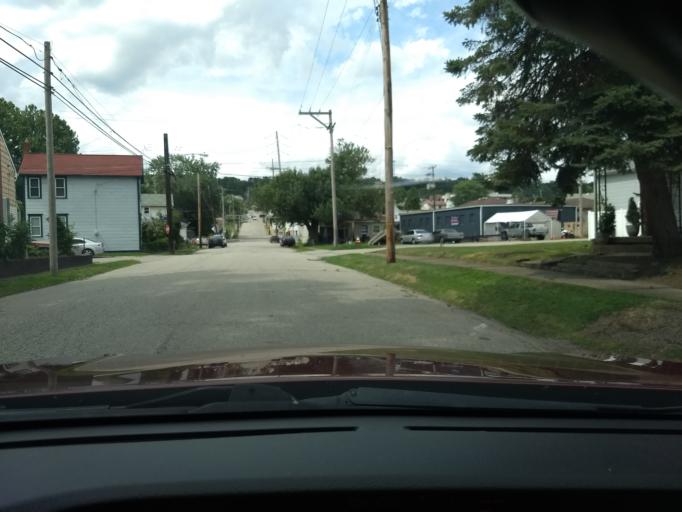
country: US
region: Pennsylvania
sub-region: Allegheny County
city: Blawnox
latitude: 40.4884
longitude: -79.8634
